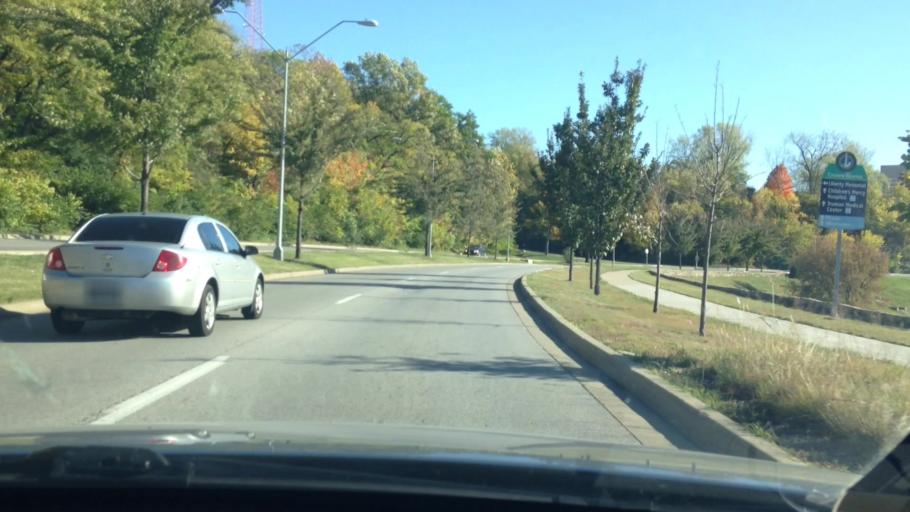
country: US
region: Missouri
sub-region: Jackson County
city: Kansas City
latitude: 39.0764
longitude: -94.5905
